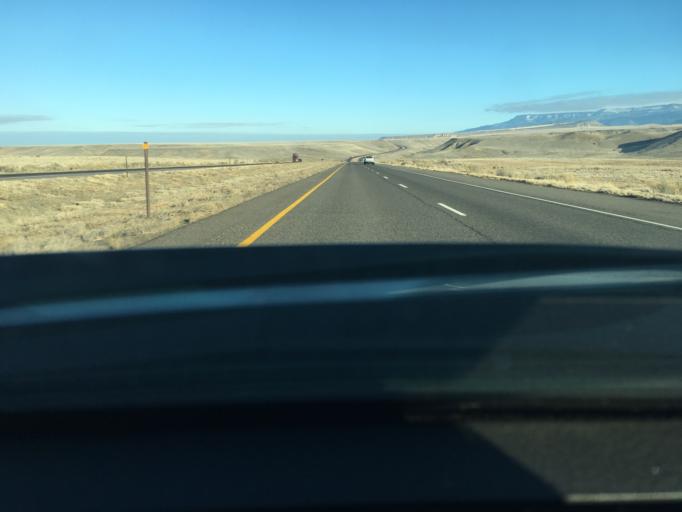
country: US
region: Colorado
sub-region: Delta County
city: Delta
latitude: 38.8171
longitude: -108.2961
